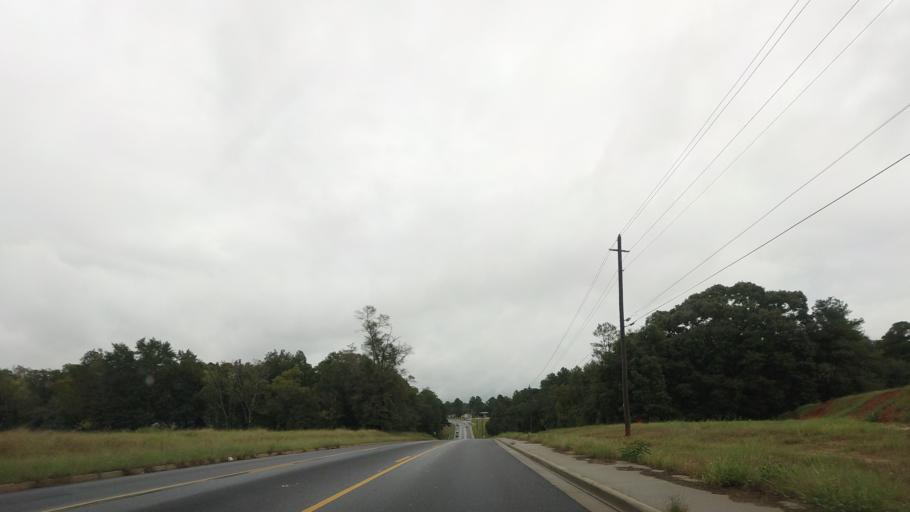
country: US
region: Georgia
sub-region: Houston County
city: Centerville
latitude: 32.5716
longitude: -83.6582
